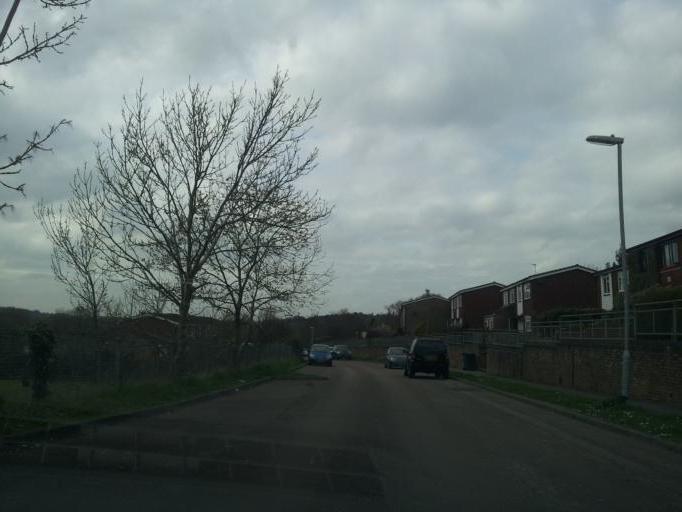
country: GB
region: England
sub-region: Essex
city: Roydon
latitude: 51.7886
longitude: 0.0119
